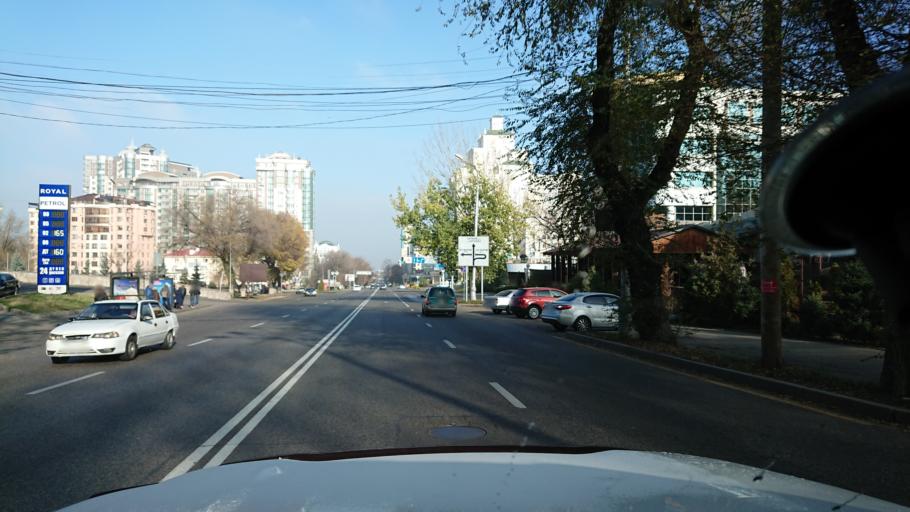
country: KZ
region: Almaty Qalasy
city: Almaty
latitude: 43.2273
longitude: 76.9612
